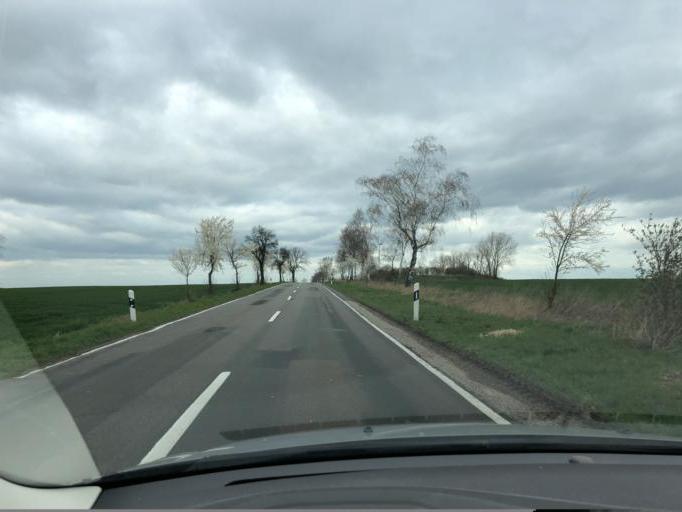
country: DE
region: Saxony-Anhalt
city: Muschwitz
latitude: 51.2194
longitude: 12.1403
